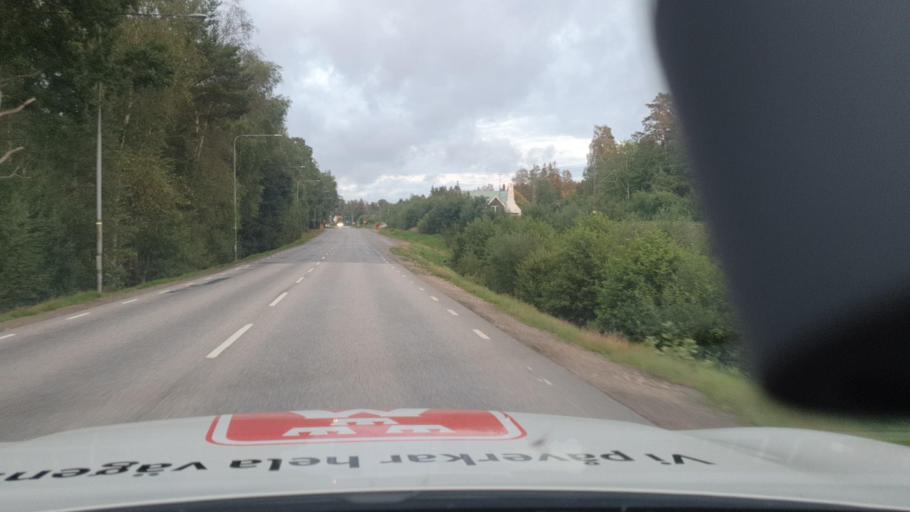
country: SE
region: Vaestra Goetaland
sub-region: Harryda Kommun
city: Hindas
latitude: 57.7048
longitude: 12.4467
